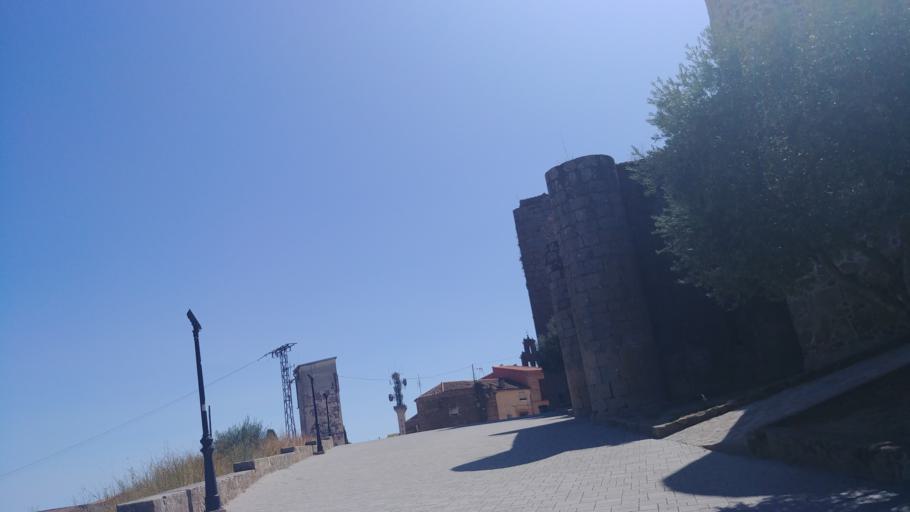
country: ES
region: Castille-La Mancha
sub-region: Province of Toledo
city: Oropesa
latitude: 39.9205
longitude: -5.1739
